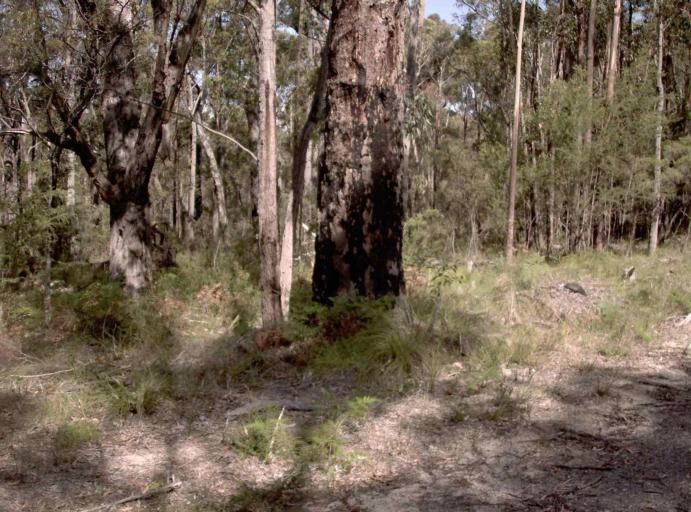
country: AU
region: New South Wales
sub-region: Bega Valley
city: Eden
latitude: -37.5391
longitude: 149.6962
